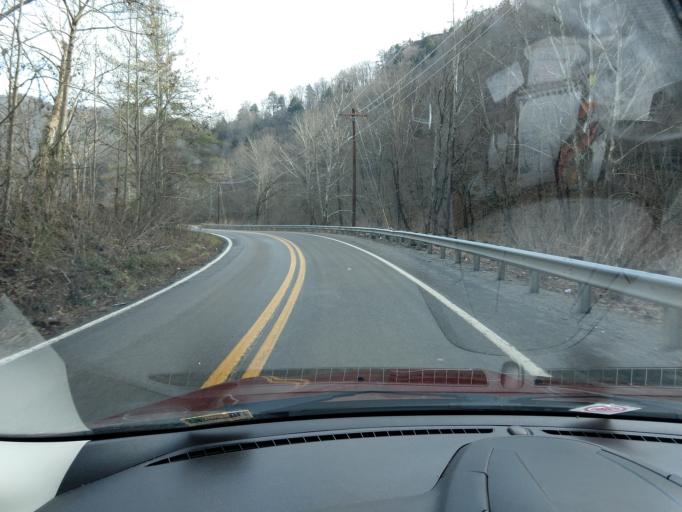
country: US
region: West Virginia
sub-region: McDowell County
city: Welch
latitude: 37.3396
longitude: -81.7152
